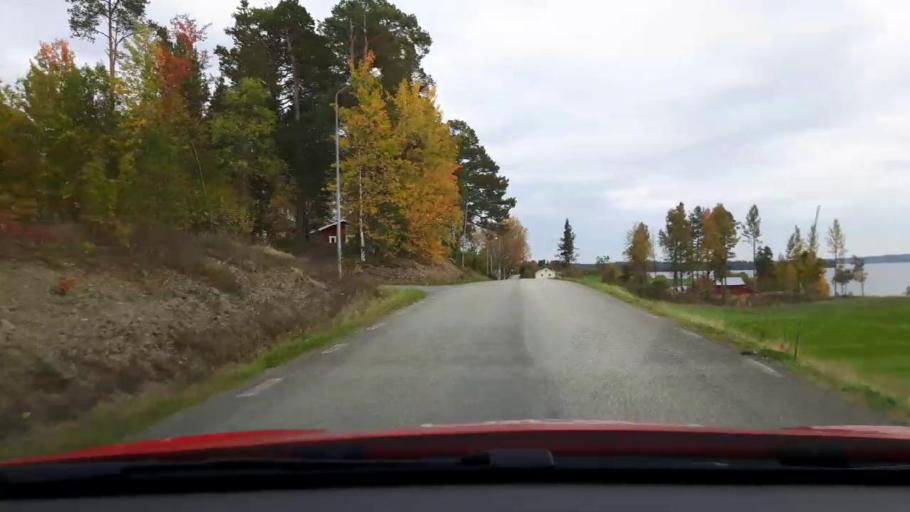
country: SE
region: Jaemtland
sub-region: Krokoms Kommun
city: Valla
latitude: 63.2498
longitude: 14.0376
